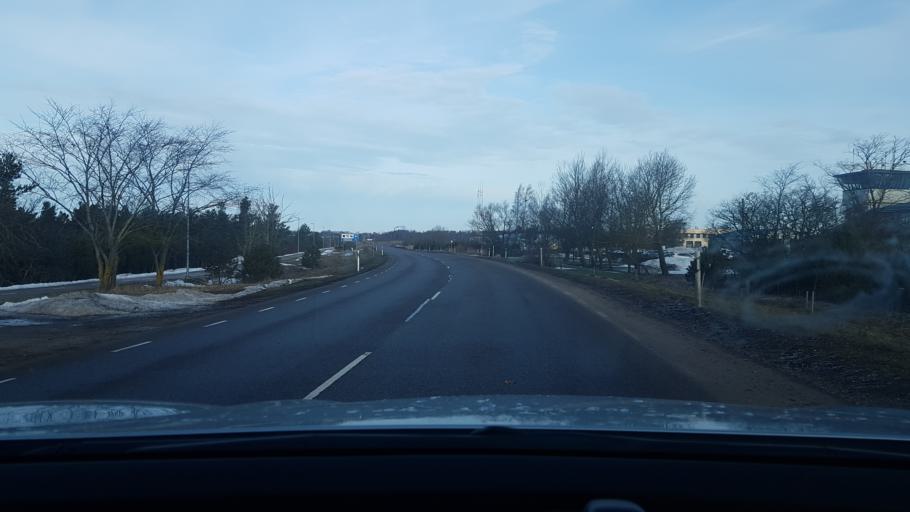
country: EE
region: Saare
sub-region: Kuressaare linn
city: Kuressaare
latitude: 58.2310
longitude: 22.5046
